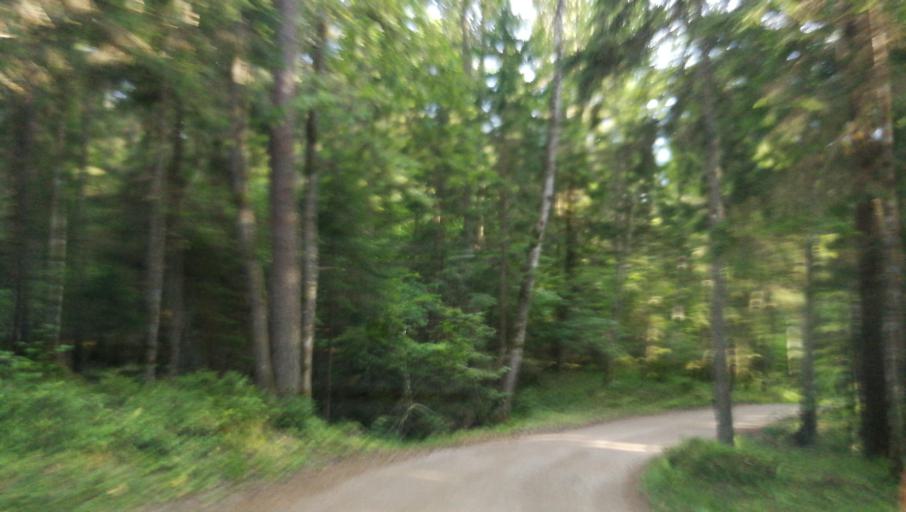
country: LV
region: Cesu Rajons
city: Cesis
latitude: 57.2893
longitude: 25.2129
